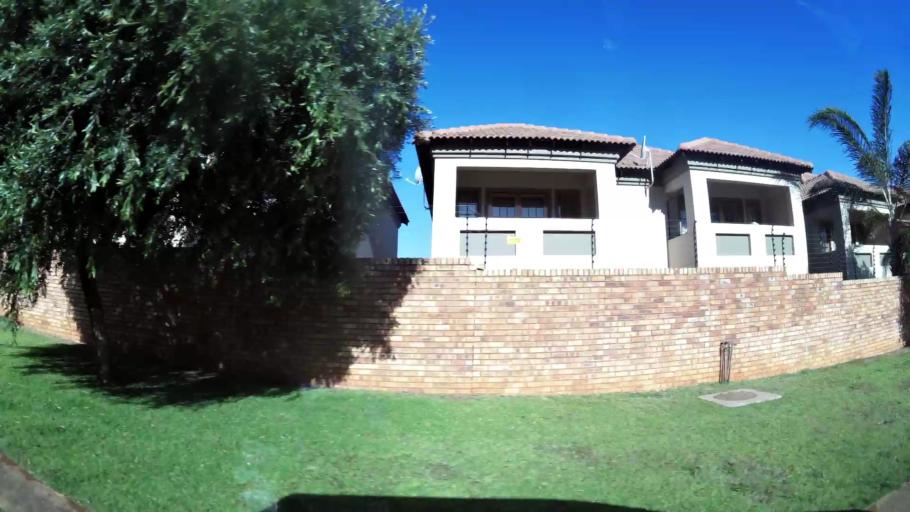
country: ZA
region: Gauteng
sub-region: City of Tshwane Metropolitan Municipality
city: Pretoria
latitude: -25.6993
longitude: 28.2775
